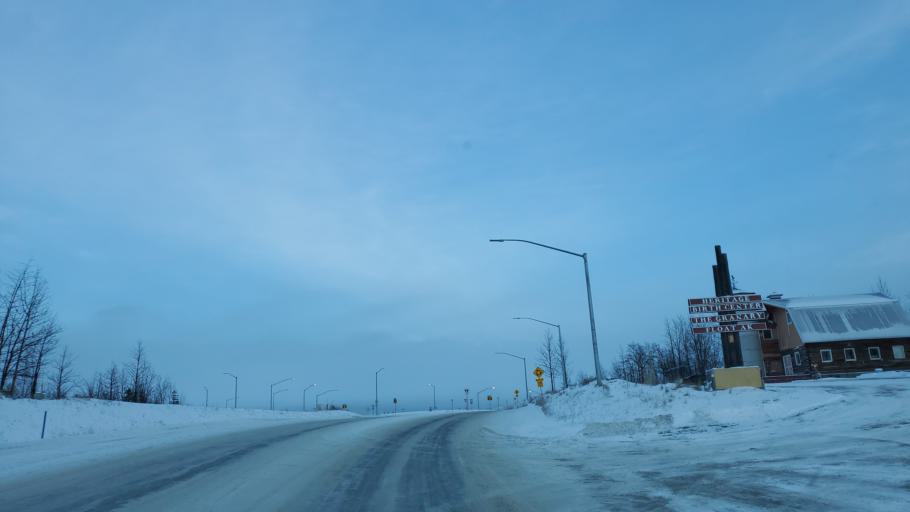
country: US
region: Alaska
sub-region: Matanuska-Susitna Borough
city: Gateway
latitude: 61.5610
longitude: -149.2707
